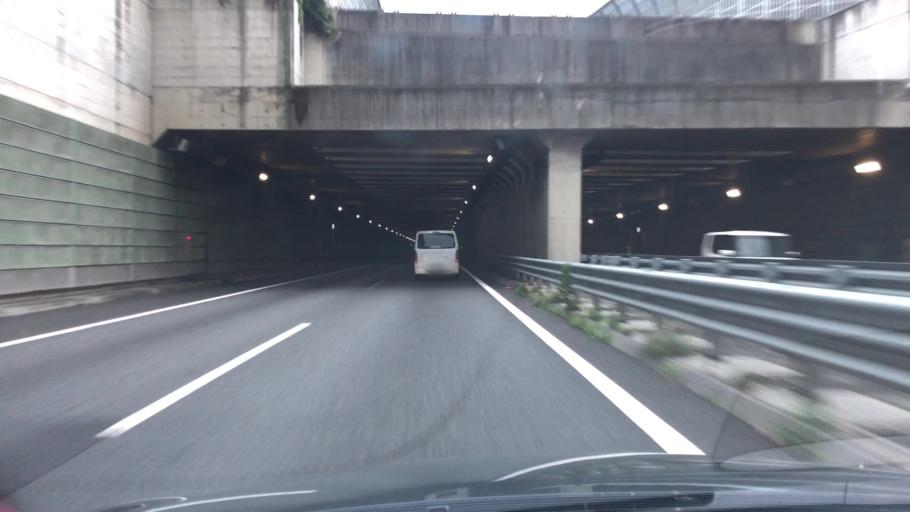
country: JP
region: Tokyo
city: Fussa
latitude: 35.7315
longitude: 139.2830
